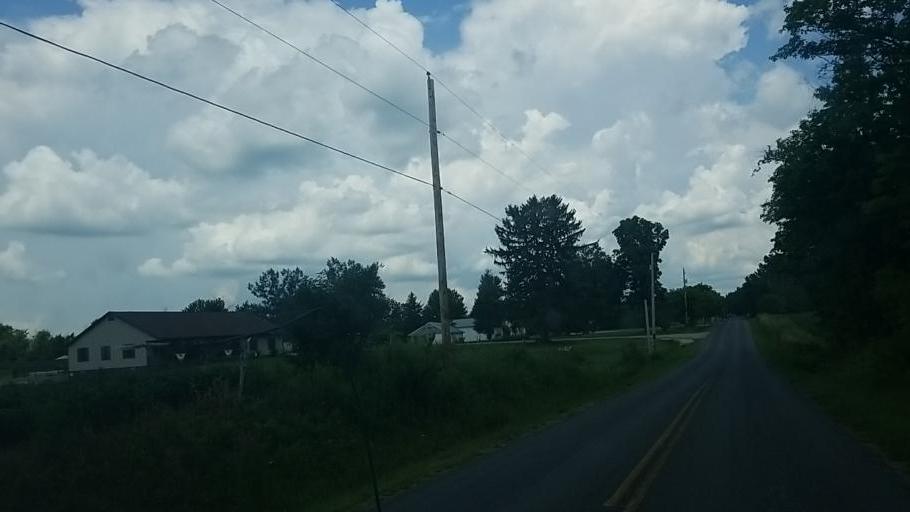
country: US
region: Ohio
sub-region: Medina County
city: Lodi
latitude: 41.0804
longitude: -82.0760
